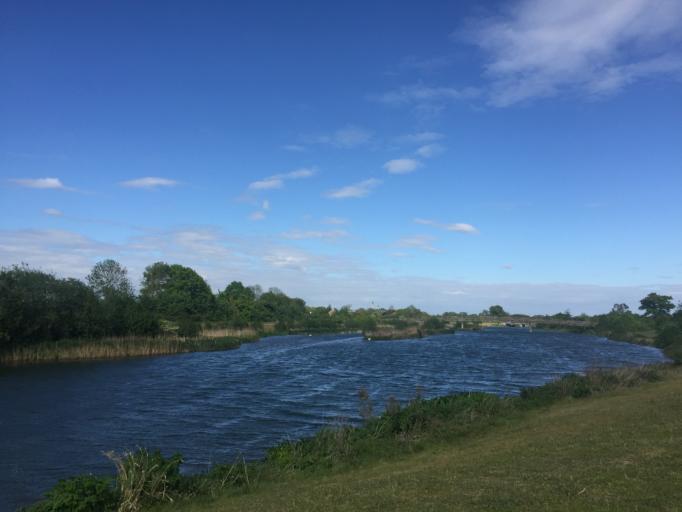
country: GB
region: England
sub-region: Royal Borough of Windsor and Maidenhead
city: Bray
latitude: 51.5057
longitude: -0.6702
